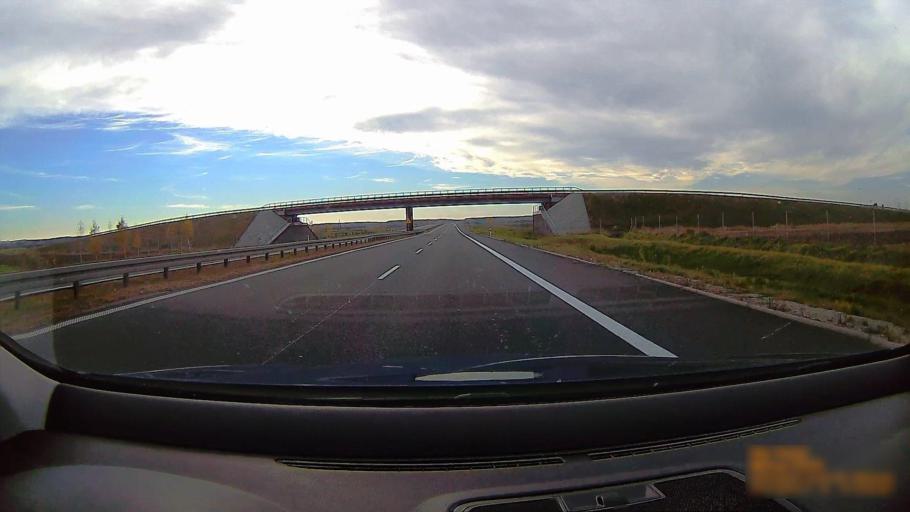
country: PL
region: Greater Poland Voivodeship
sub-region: Powiat ostrowski
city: Przygodzice
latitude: 51.5918
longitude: 17.8501
